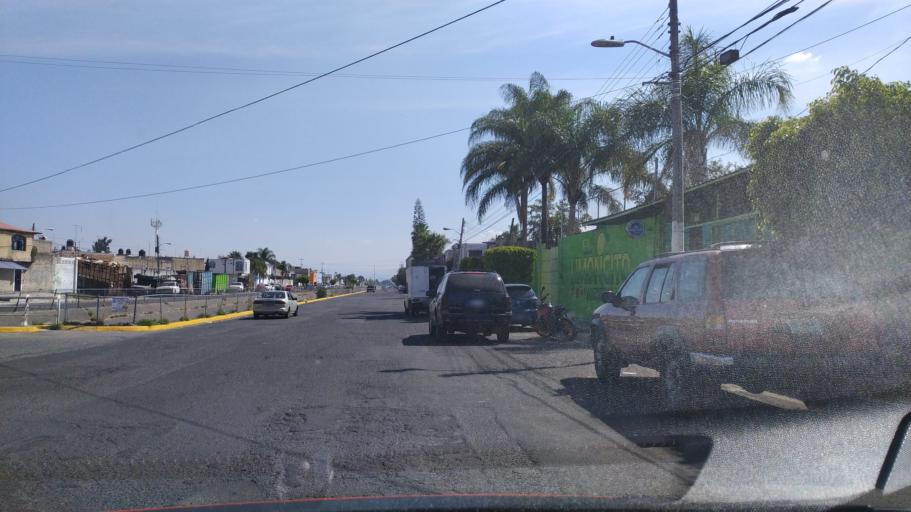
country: MX
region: Jalisco
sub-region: Tlajomulco de Zuniga
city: Palomar
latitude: 20.6477
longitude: -103.4502
